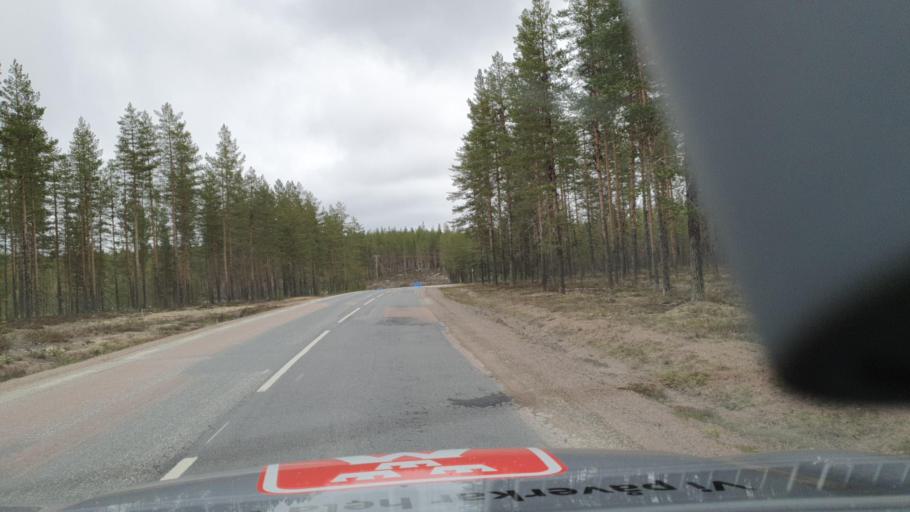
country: SE
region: Vaesternorrland
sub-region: Solleftea Kommun
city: Solleftea
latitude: 63.6408
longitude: 17.4106
